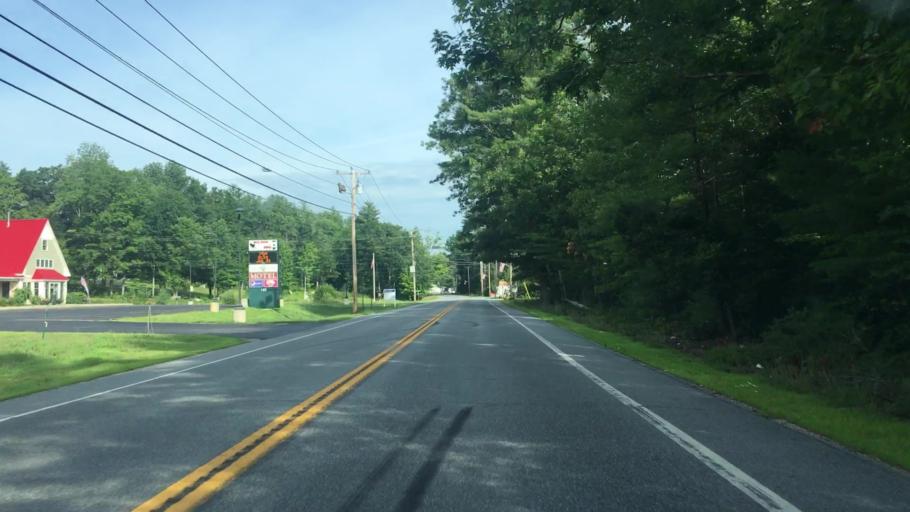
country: US
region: Maine
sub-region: York County
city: Cornish
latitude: 43.8005
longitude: -70.7870
